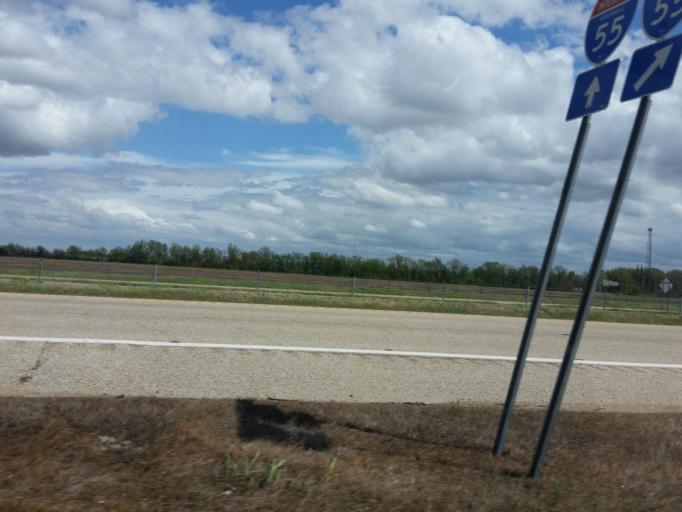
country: US
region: Arkansas
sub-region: Crittenden County
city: Marion
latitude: 35.3959
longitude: -90.2759
